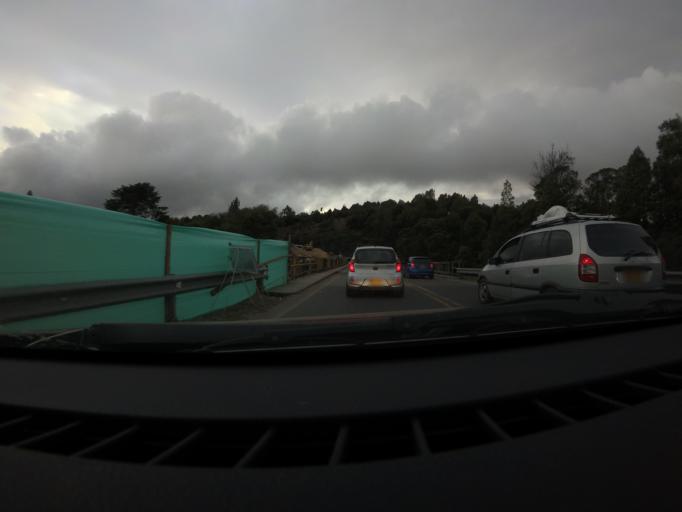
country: CO
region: Boyaca
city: Samaca
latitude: 5.4516
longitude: -73.4308
